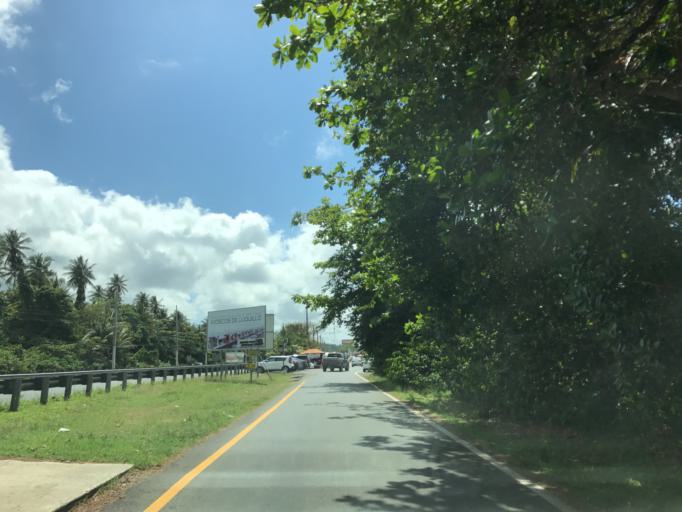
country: PR
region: Luquillo
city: Playa Fortuna
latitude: 18.3813
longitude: -65.7330
